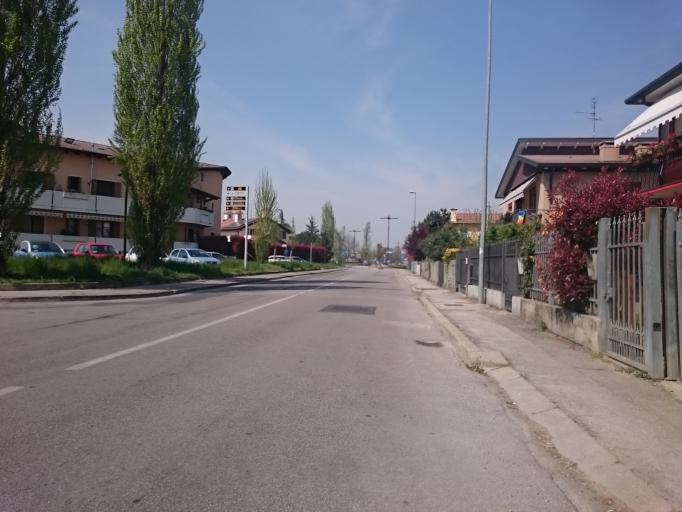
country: IT
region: Veneto
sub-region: Provincia di Padova
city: Sarmeola
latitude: 45.4252
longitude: 11.8121
